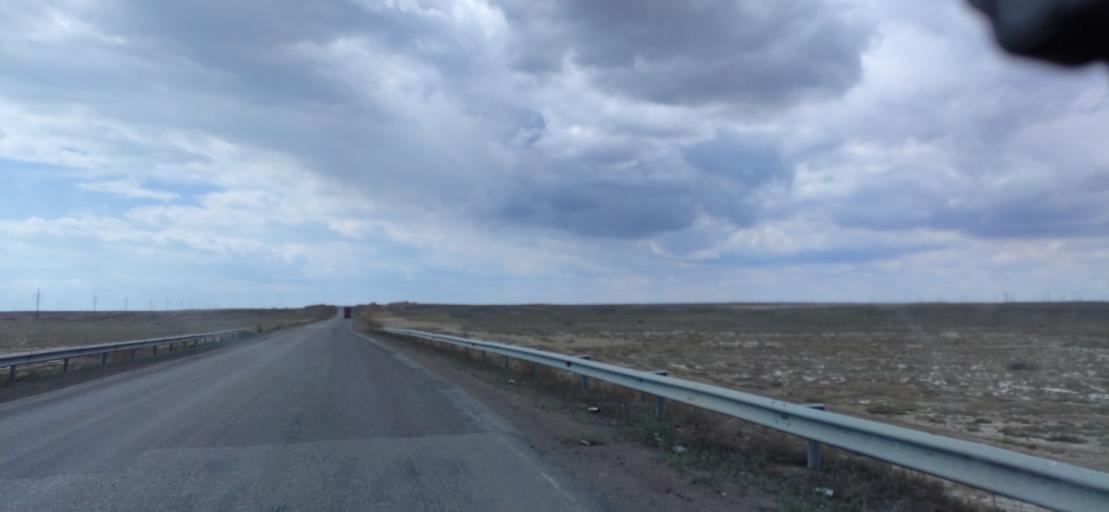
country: KZ
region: Qaraghandy
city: Saryshaghan
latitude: 46.0902
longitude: 73.6072
